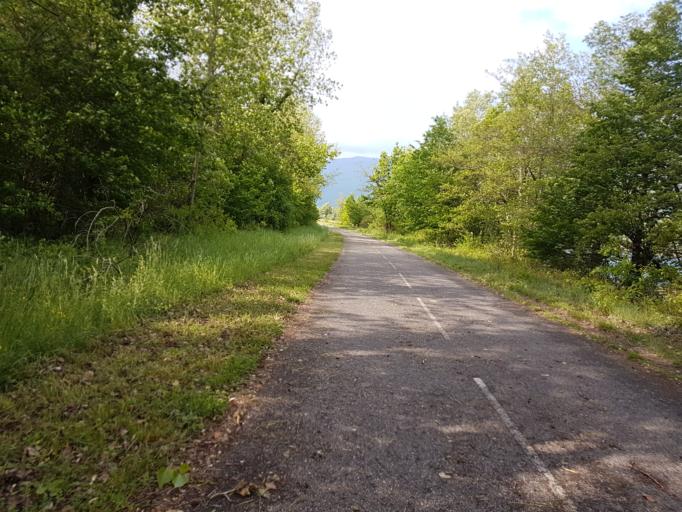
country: FR
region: Rhone-Alpes
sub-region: Departement de la Haute-Savoie
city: Versonnex
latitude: 45.9431
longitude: 5.8362
